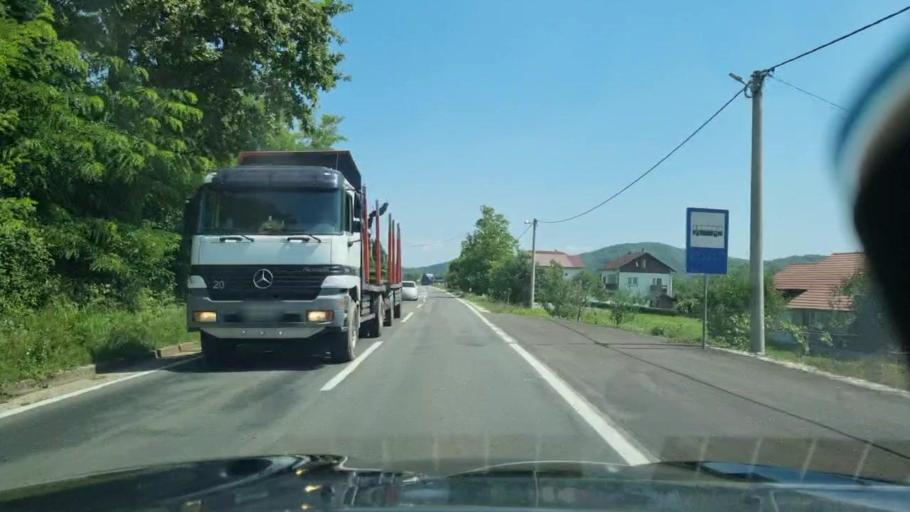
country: BA
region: Federation of Bosnia and Herzegovina
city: Sanski Most
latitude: 44.8068
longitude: 16.6452
